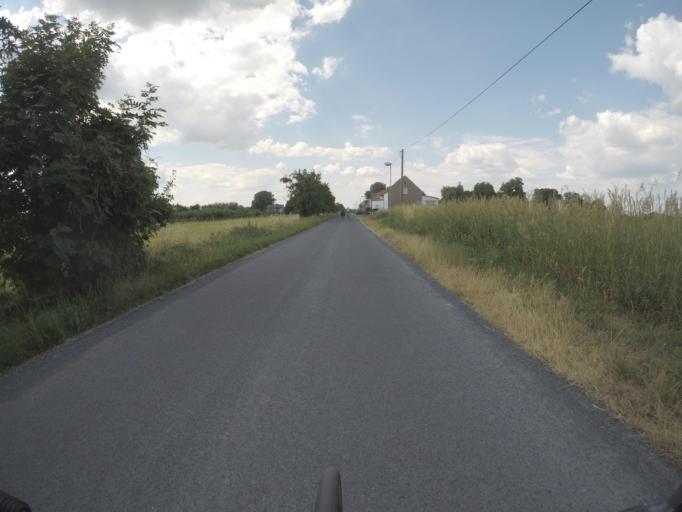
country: DE
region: Brandenburg
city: Roskow
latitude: 52.4500
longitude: 12.7672
